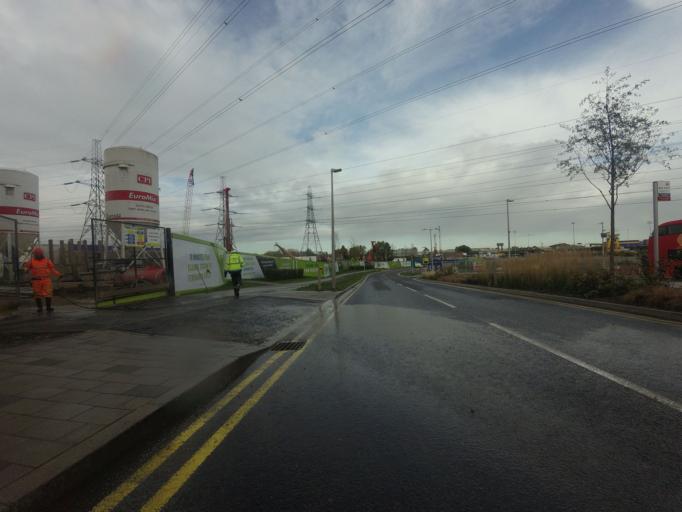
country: GB
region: England
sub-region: Greater London
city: Becontree
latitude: 51.5254
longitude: 0.1239
